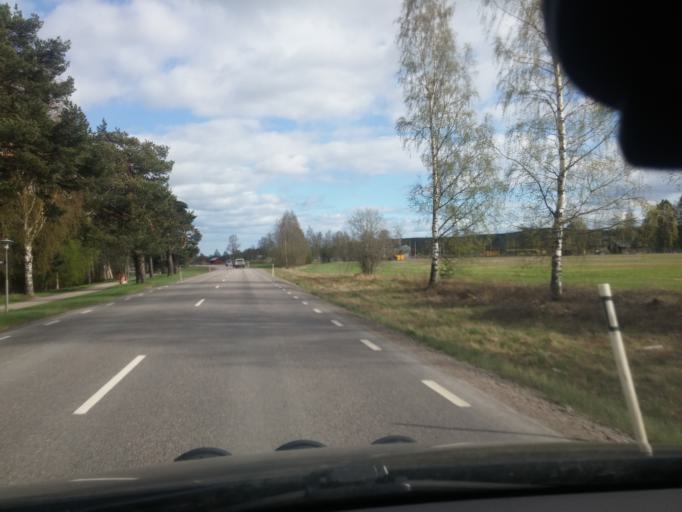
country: SE
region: Gaevleborg
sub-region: Ljusdals Kommun
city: Ljusdal
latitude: 61.8229
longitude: 16.0769
